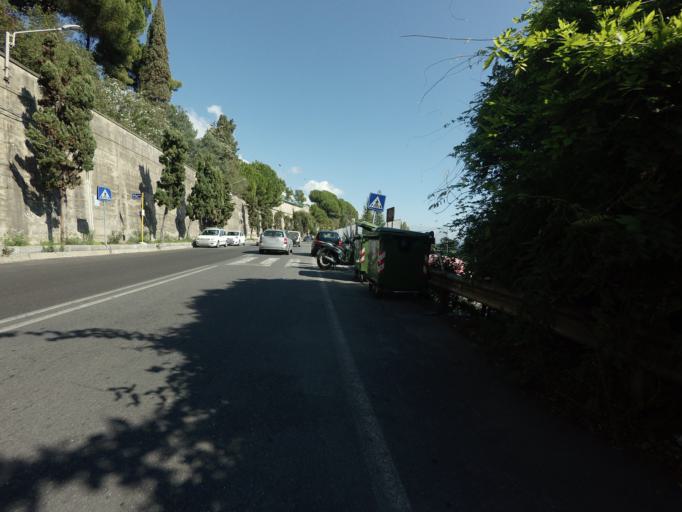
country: IT
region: Sicily
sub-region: Messina
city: Taormina
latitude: 37.8653
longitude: 15.2967
